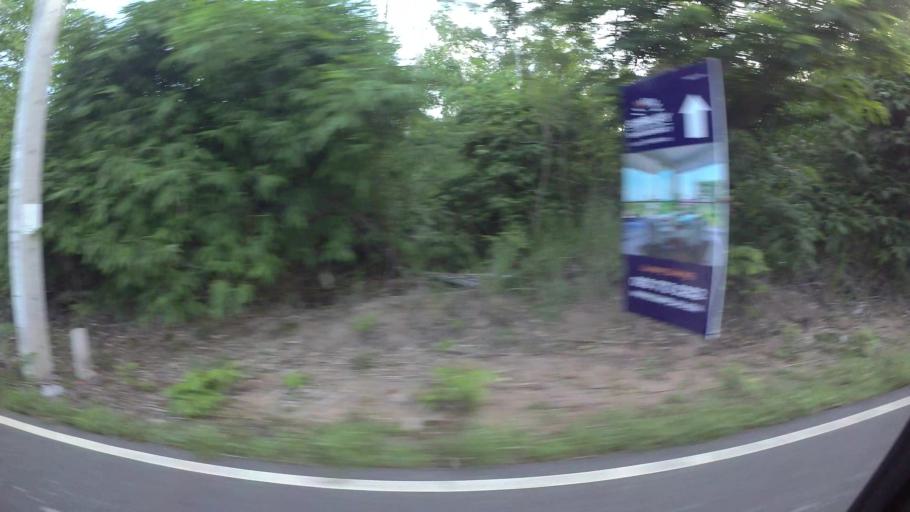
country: TH
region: Chon Buri
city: Sattahip
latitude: 12.7439
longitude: 100.9346
